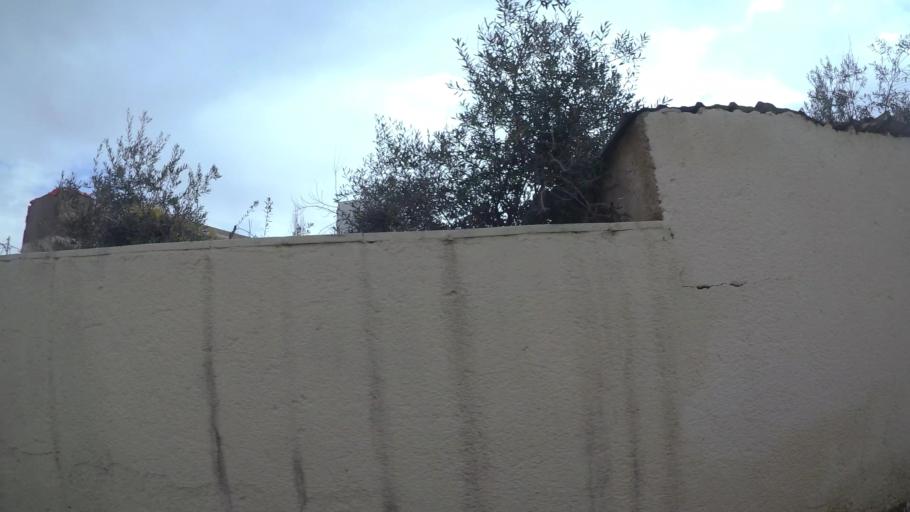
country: JO
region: Amman
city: Umm as Summaq
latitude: 31.9043
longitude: 35.8345
